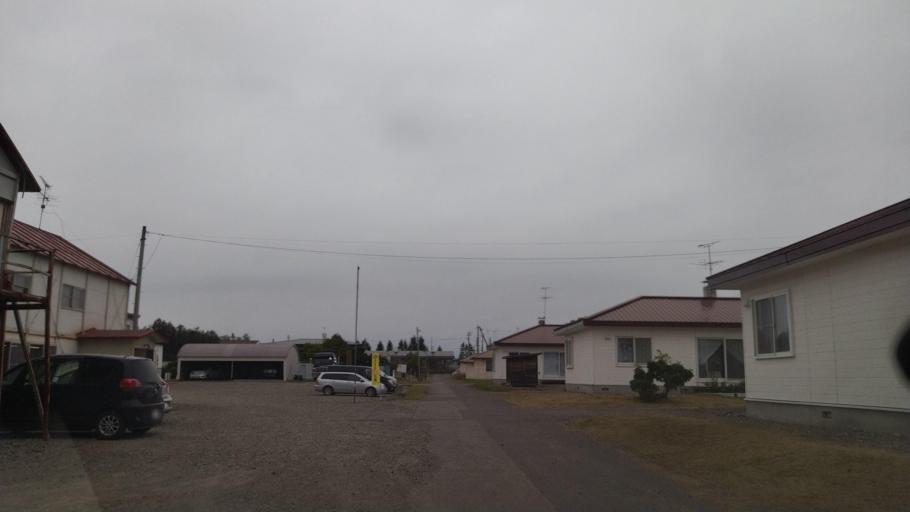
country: JP
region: Hokkaido
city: Otofuke
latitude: 43.2319
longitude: 143.2792
